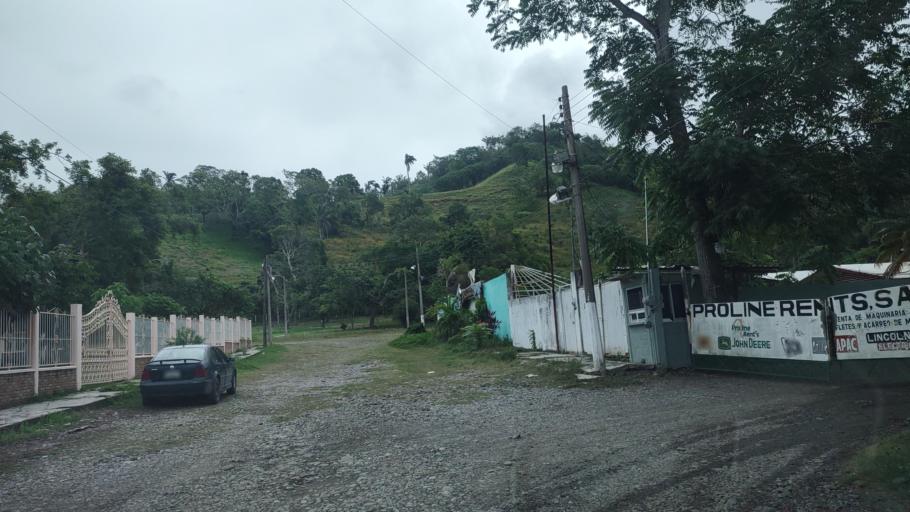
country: MX
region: Veracruz
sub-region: Papantla
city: Fraccionamiento la Florida
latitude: 20.5874
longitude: -97.4230
